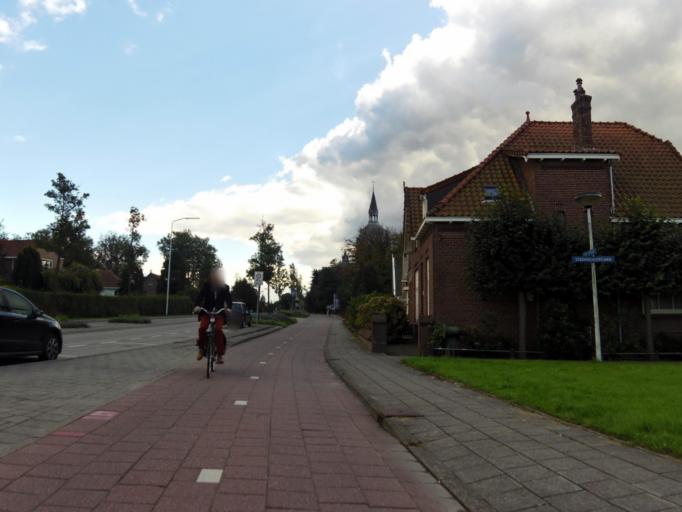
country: NL
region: South Holland
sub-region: Gemeente Leiderdorp
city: Leiderdorp
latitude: 52.1466
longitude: 4.5228
